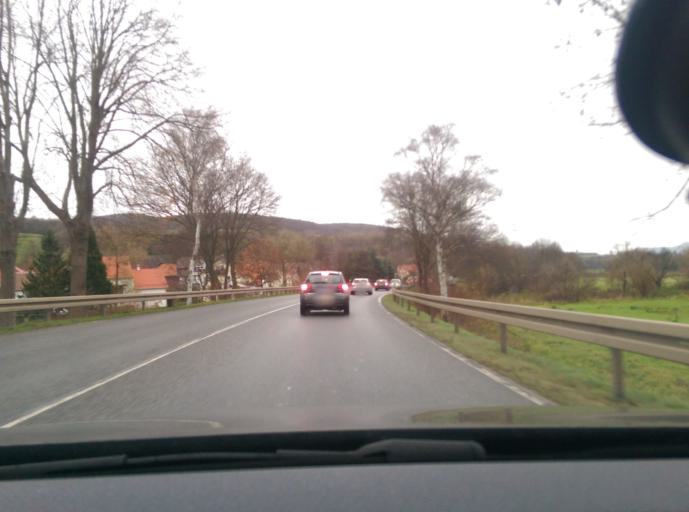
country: DE
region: Hesse
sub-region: Regierungsbezirk Kassel
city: Sontra
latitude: 51.1378
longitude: 9.9761
